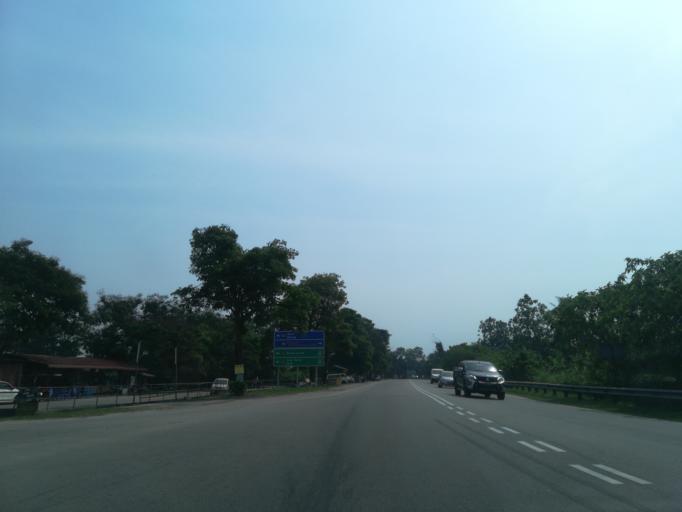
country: MY
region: Kedah
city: Kulim
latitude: 5.4284
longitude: 100.5527
